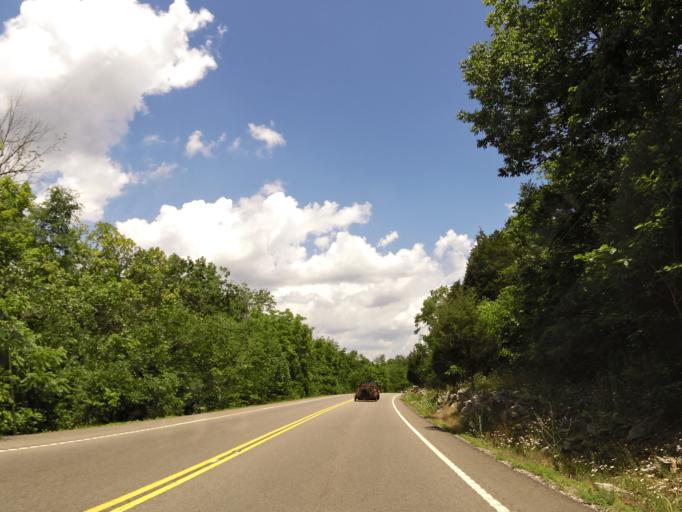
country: US
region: Tennessee
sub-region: Union County
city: Maynardville
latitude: 36.3471
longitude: -83.7392
